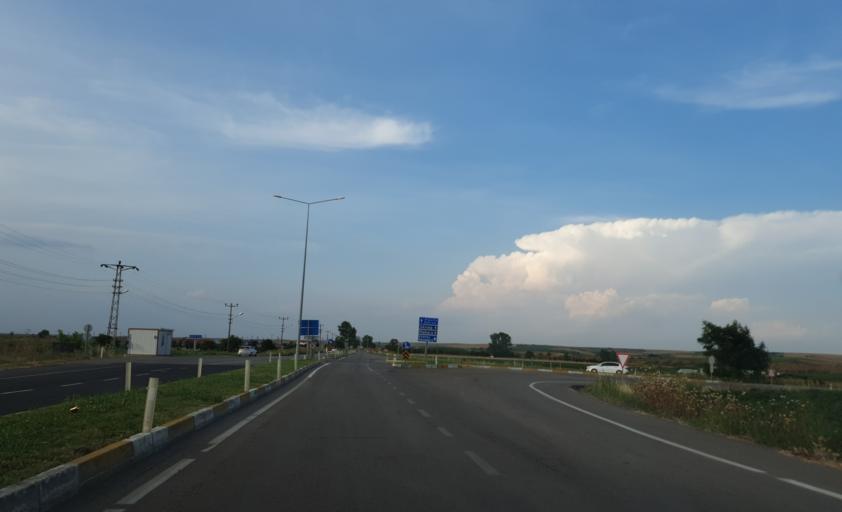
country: TR
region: Tekirdag
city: Hayrabolu
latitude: 41.2254
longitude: 27.1180
